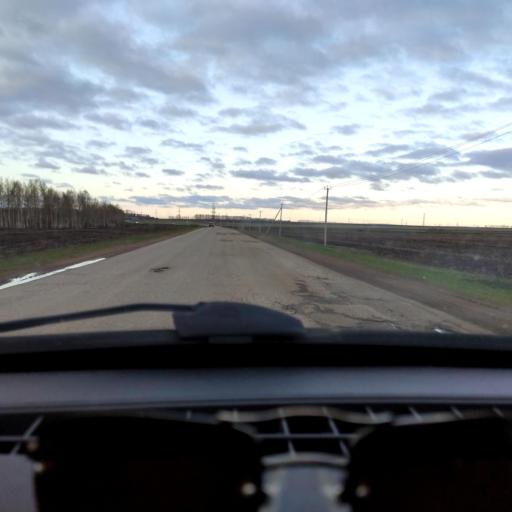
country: RU
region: Bashkortostan
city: Kabakovo
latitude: 54.5400
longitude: 56.0759
